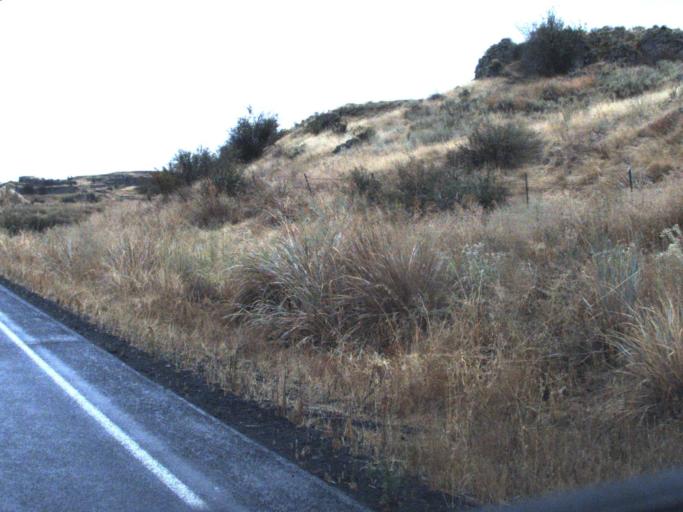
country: US
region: Washington
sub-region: Spokane County
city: Medical Lake
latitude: 47.2697
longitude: -117.9414
